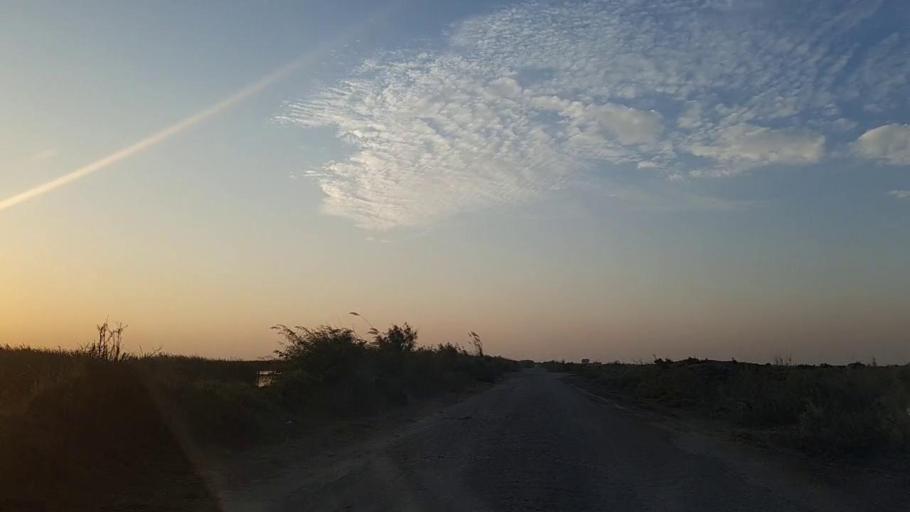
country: PK
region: Sindh
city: Chuhar Jamali
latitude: 24.4659
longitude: 68.0989
